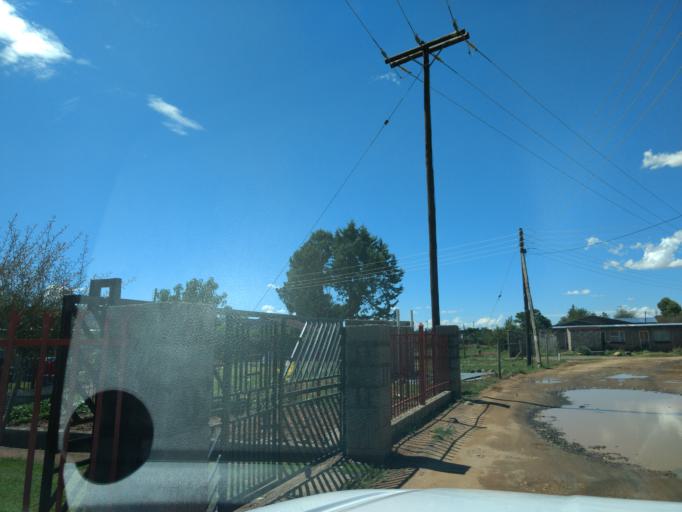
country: LS
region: Maseru
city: Maseru
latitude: -29.3704
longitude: 27.5115
